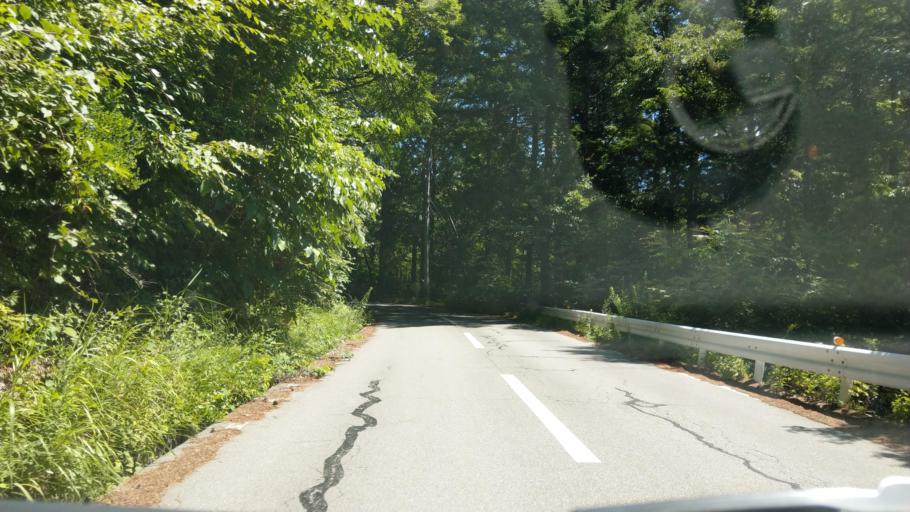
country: JP
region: Nagano
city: Komoro
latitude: 36.3688
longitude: 138.4604
